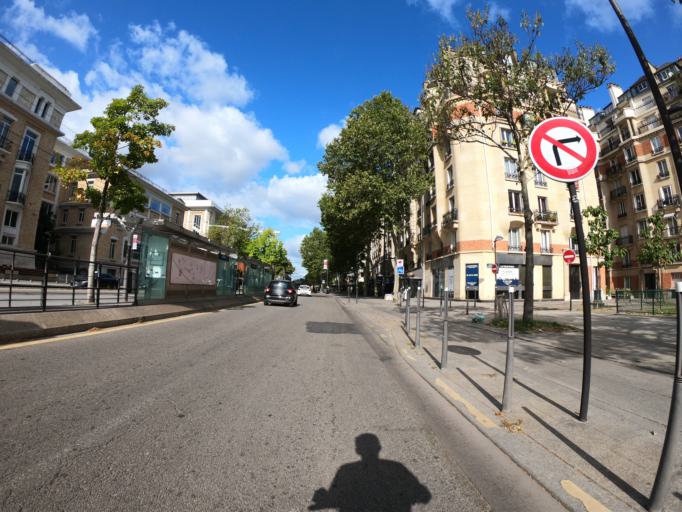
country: FR
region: Ile-de-France
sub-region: Departement des Hauts-de-Seine
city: Vanves
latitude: 48.8346
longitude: 2.2838
